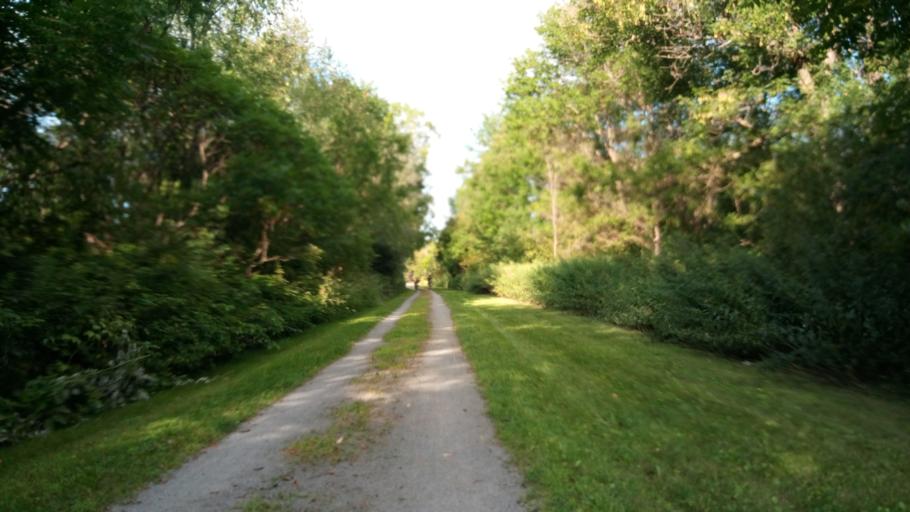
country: US
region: New York
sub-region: Monroe County
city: Honeoye Falls
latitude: 42.9956
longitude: -77.5141
